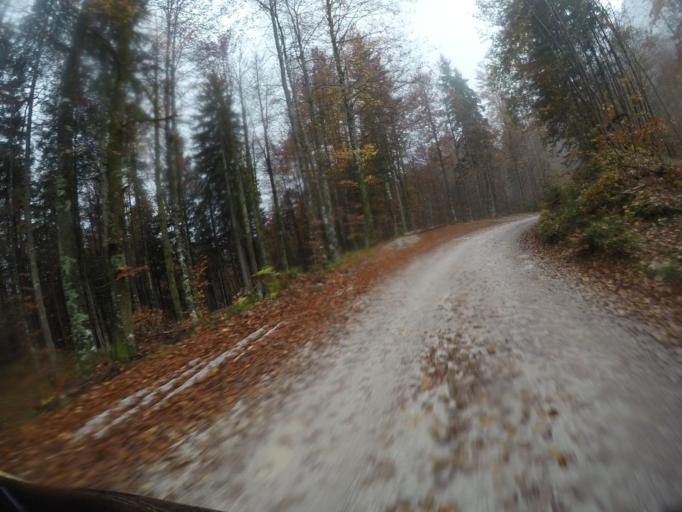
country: SI
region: Kranjska Gora
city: Mojstrana
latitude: 46.4257
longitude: 13.8681
